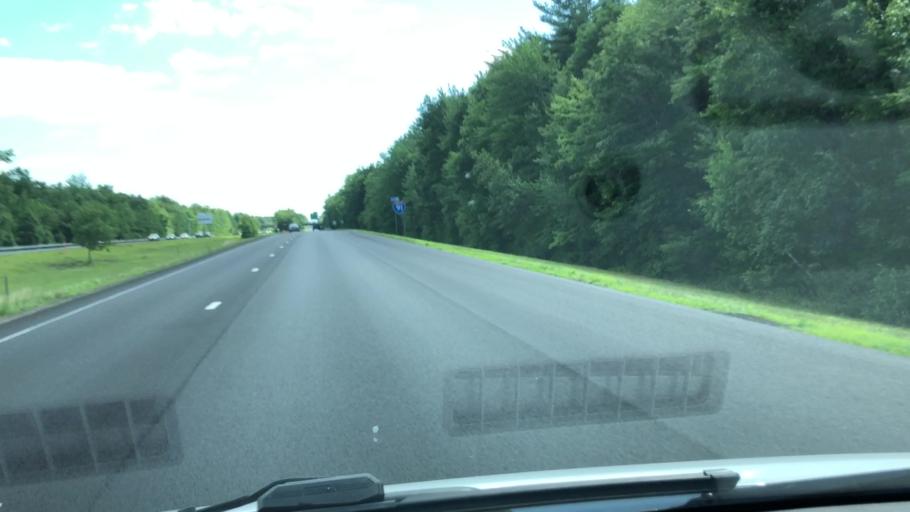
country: US
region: Massachusetts
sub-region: Franklin County
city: Whately
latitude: 42.4528
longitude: -72.6186
